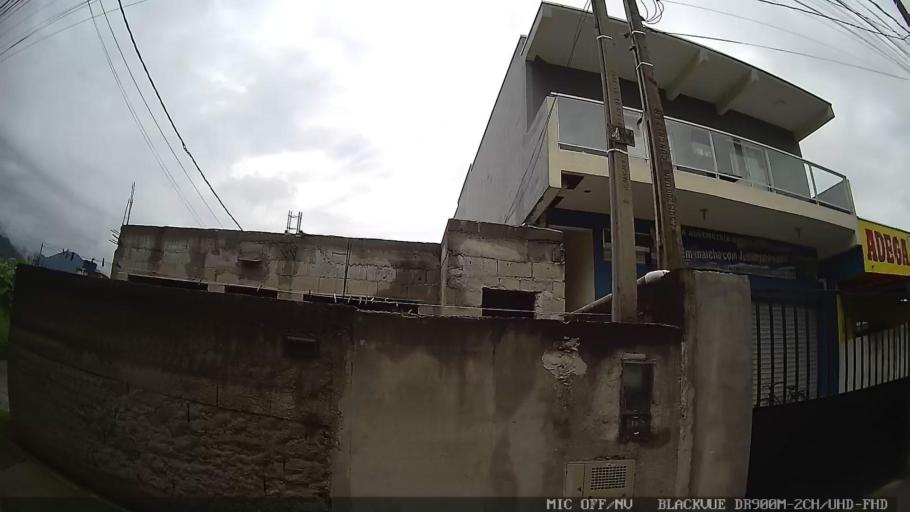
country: BR
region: Sao Paulo
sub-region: Sao Sebastiao
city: Sao Sebastiao
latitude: -23.7223
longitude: -45.4390
